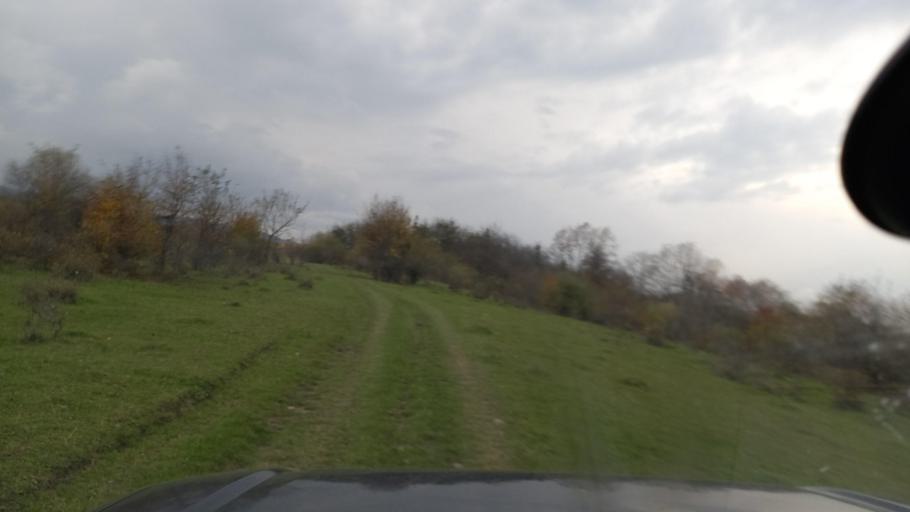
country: RU
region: Krasnodarskiy
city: Gubskaya
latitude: 44.2881
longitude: 40.5399
